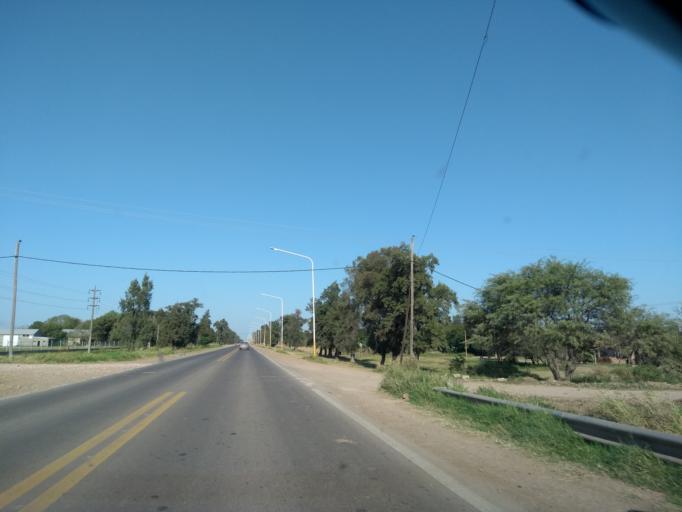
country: AR
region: Chaco
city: Presidencia Roque Saenz Pena
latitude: -26.7865
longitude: -60.4070
